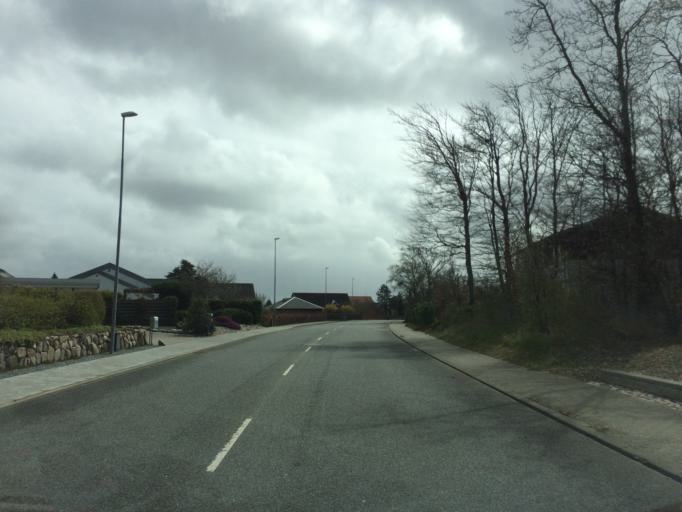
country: DK
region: South Denmark
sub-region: Fano Kommune
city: Nordby
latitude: 55.5340
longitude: 8.3474
